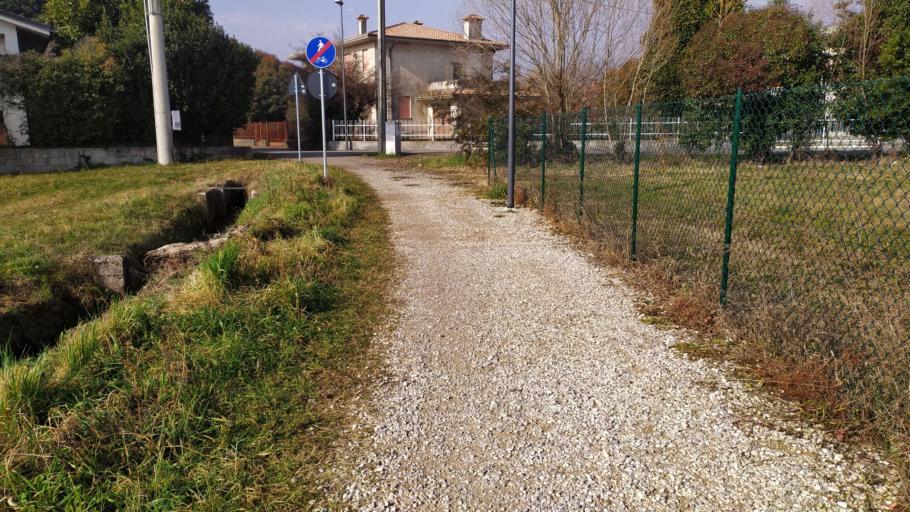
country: IT
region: Veneto
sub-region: Provincia di Treviso
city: Volpago del Montello
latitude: 45.7799
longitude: 12.1151
